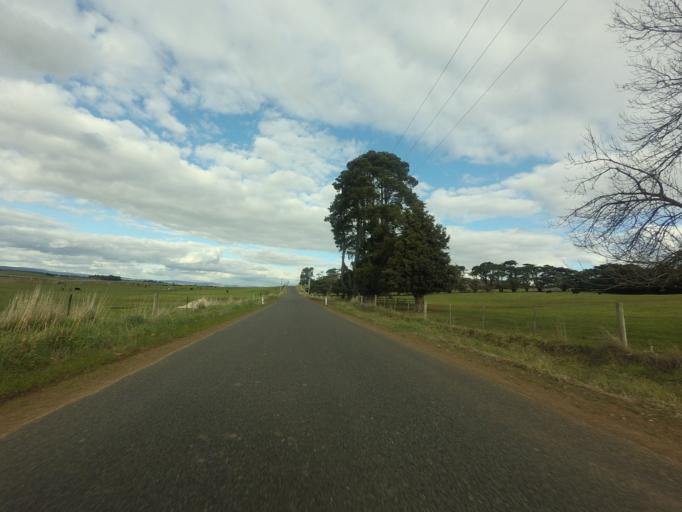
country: AU
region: Tasmania
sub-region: Northern Midlands
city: Evandale
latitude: -41.9035
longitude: 147.3546
